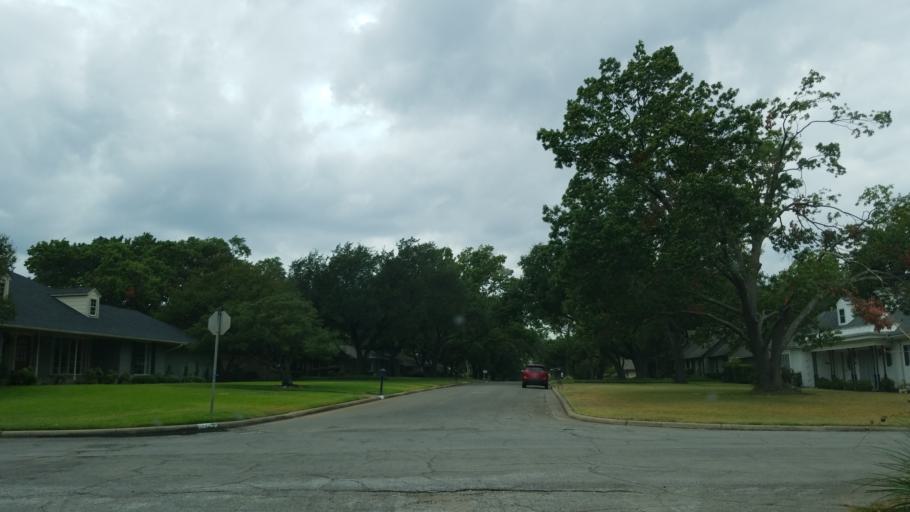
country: US
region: Texas
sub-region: Dallas County
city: Richardson
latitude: 32.9441
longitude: -96.7730
